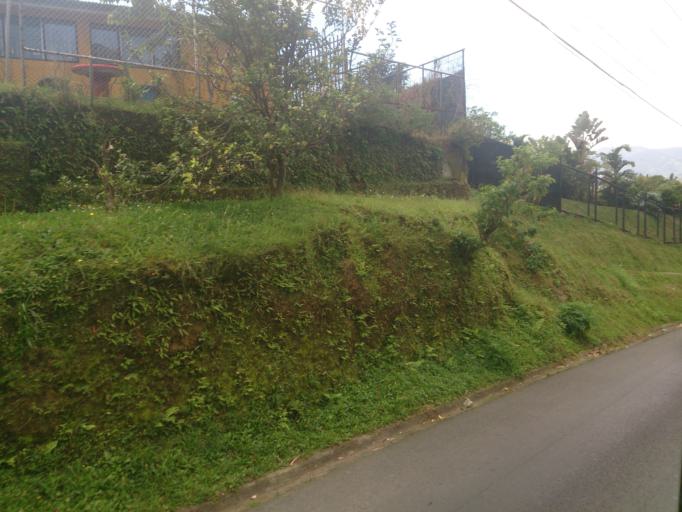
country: CR
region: San Jose
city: Granadilla
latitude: 9.9272
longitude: -84.0137
